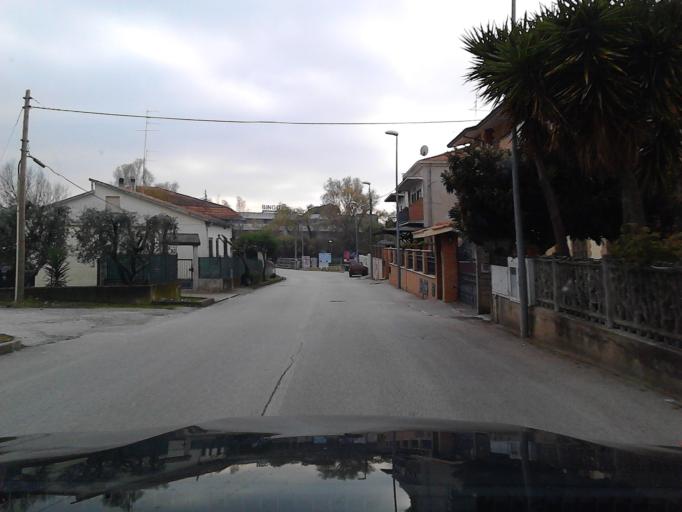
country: IT
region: Abruzzo
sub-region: Provincia di Teramo
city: Villa Rosa
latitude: 42.8354
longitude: 13.8935
